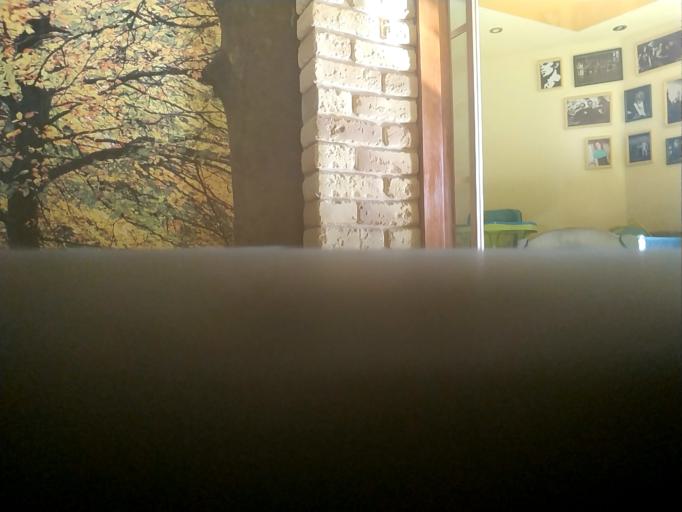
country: RU
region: Smolensk
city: Temkino
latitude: 54.9498
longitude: 34.9567
